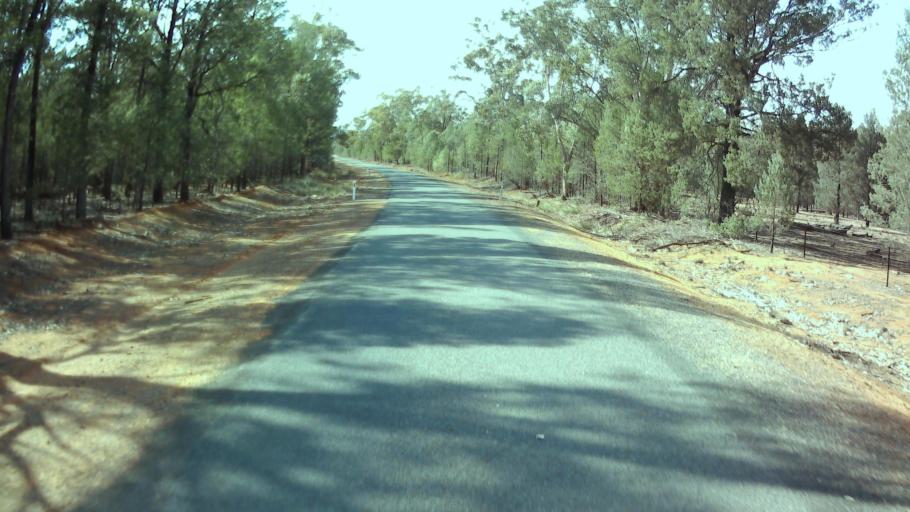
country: AU
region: New South Wales
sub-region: Weddin
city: Grenfell
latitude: -33.7233
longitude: 148.0296
